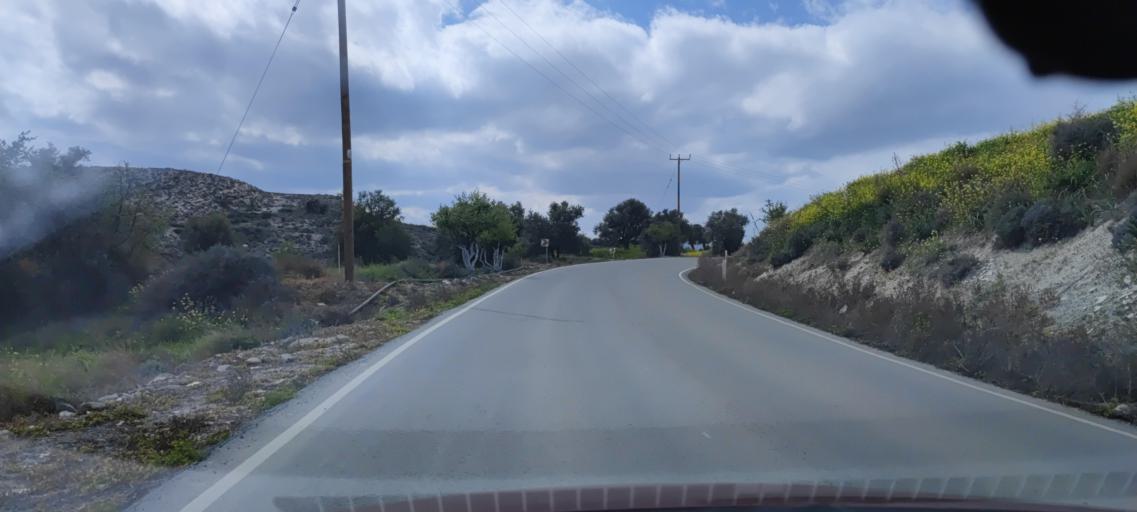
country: CY
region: Lefkosia
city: Pera
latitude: 35.0194
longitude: 33.3008
